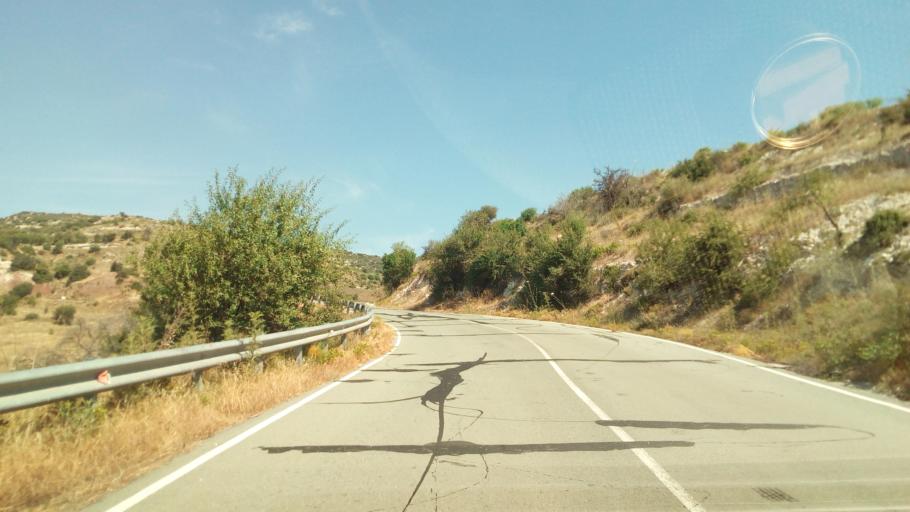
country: CY
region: Limassol
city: Pachna
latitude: 34.8003
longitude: 32.6874
